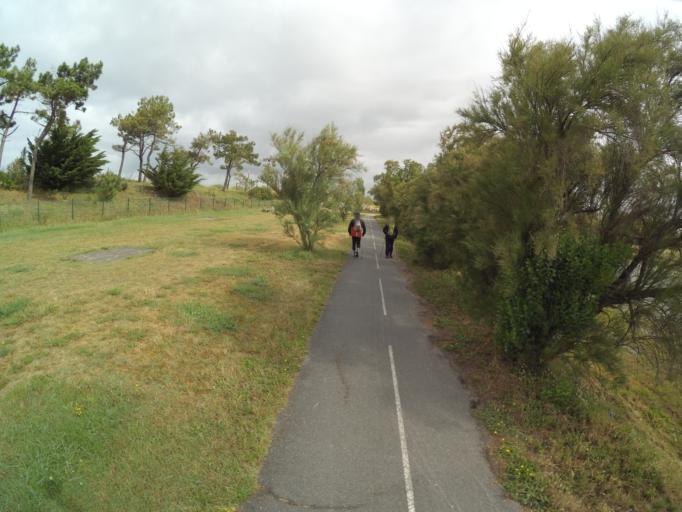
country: FR
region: Poitou-Charentes
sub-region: Departement de la Charente-Maritime
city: Aytre
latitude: 46.1178
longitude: -1.1234
